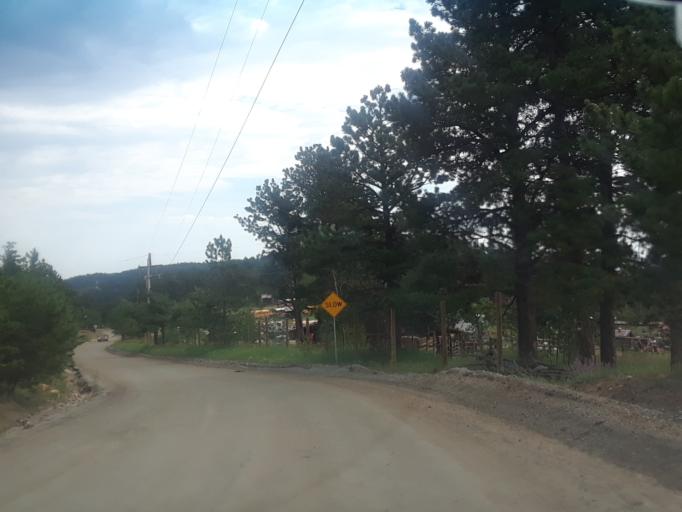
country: US
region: Colorado
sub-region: Boulder County
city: Nederland
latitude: 40.0583
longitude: -105.4190
